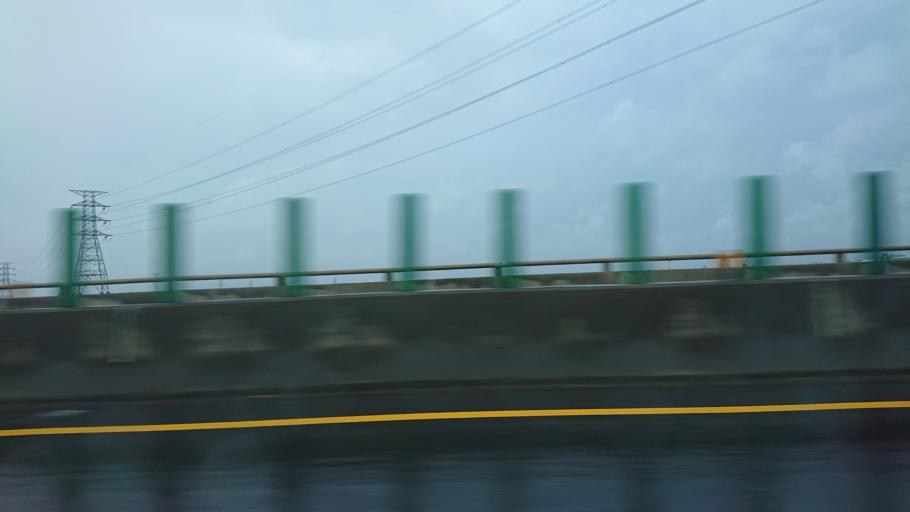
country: TW
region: Taiwan
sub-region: Changhua
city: Chang-hua
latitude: 24.1240
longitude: 120.4386
